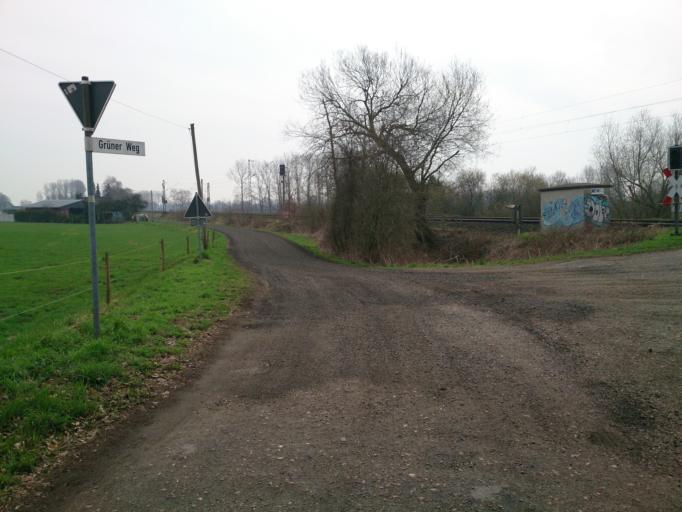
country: DE
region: Lower Saxony
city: Buxtehude
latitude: 53.4699
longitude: 9.7279
